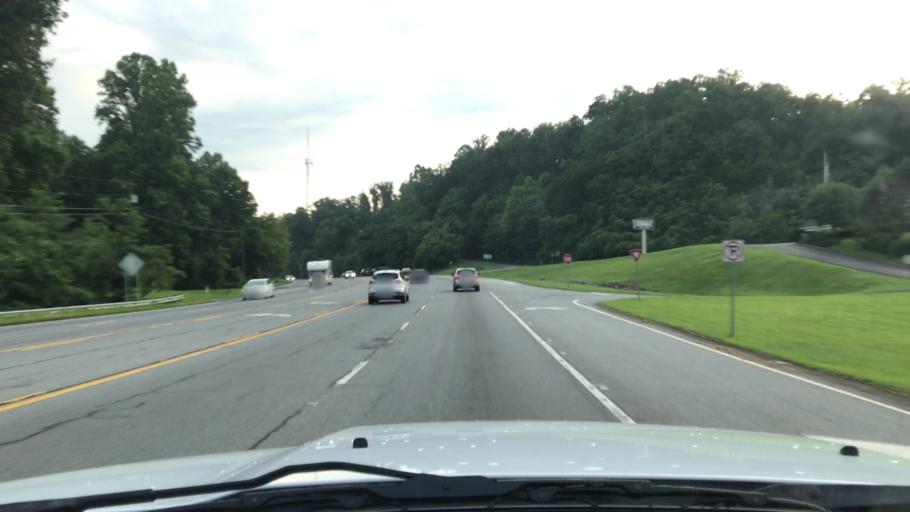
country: US
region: Georgia
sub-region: Fannin County
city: Blue Ridge
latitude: 34.8714
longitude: -84.3273
